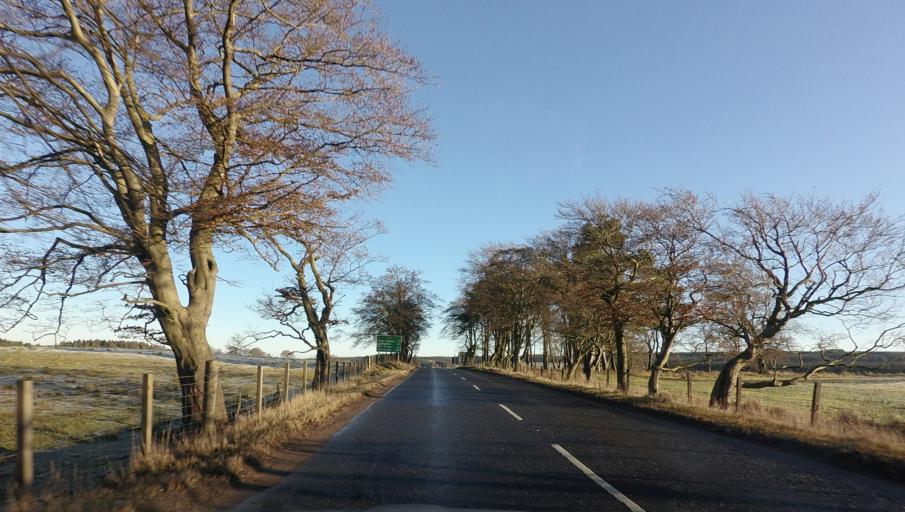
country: GB
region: Scotland
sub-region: West Lothian
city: Fauldhouse
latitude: 55.8084
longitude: -3.7389
